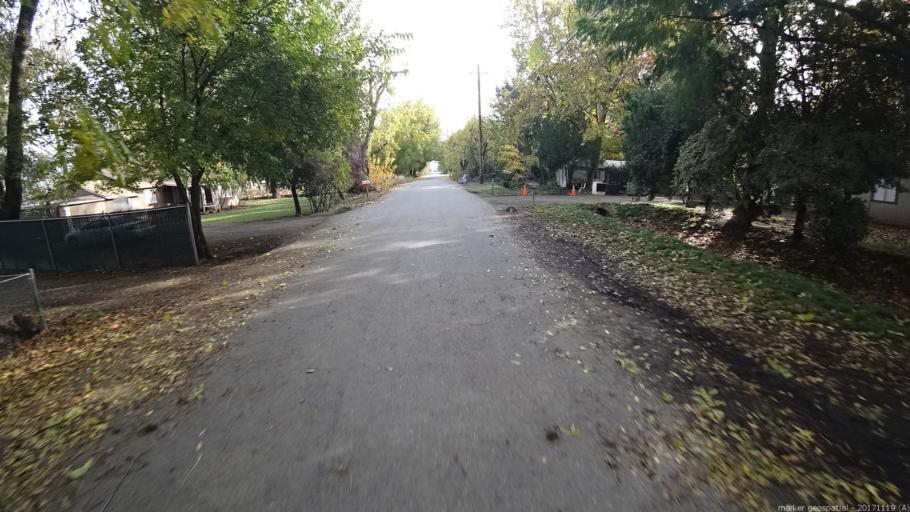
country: US
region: California
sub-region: Shasta County
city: Anderson
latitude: 40.5147
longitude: -122.3413
